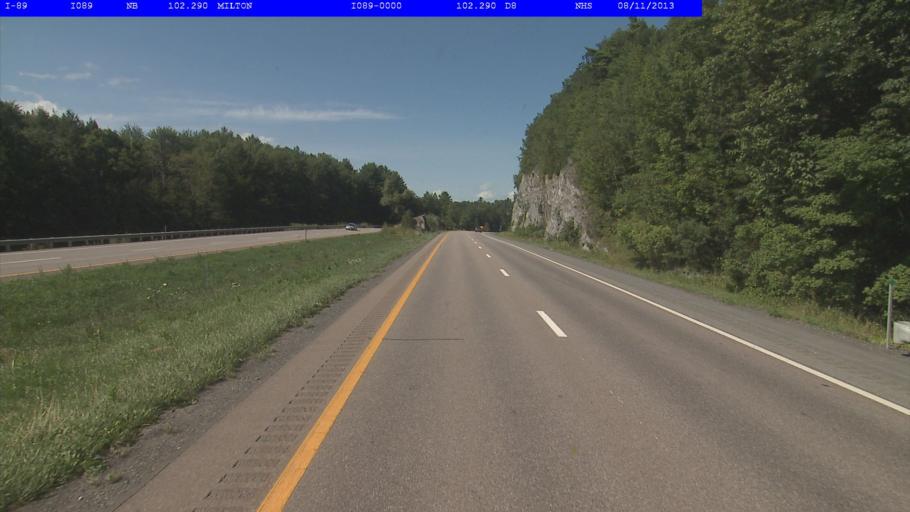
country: US
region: Vermont
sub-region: Chittenden County
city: Milton
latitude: 44.6464
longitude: -73.1400
